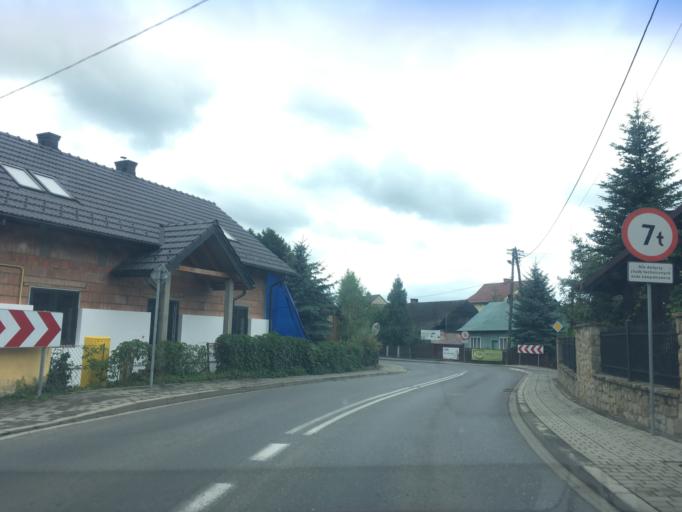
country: PL
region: Lesser Poland Voivodeship
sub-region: Powiat myslenicki
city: Dobczyce
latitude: 49.8777
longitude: 20.0990
